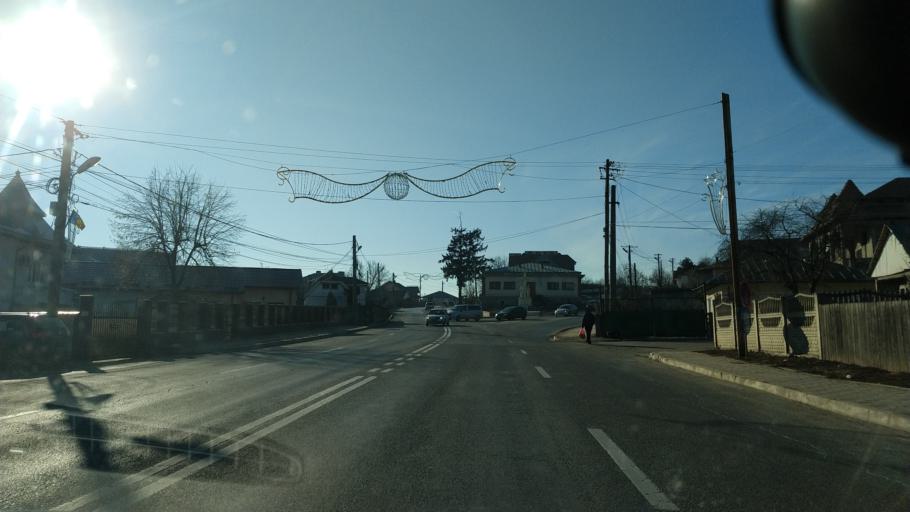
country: RO
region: Iasi
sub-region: Comuna Targu Frumos
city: Targu Frumos
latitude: 47.2047
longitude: 27.0080
